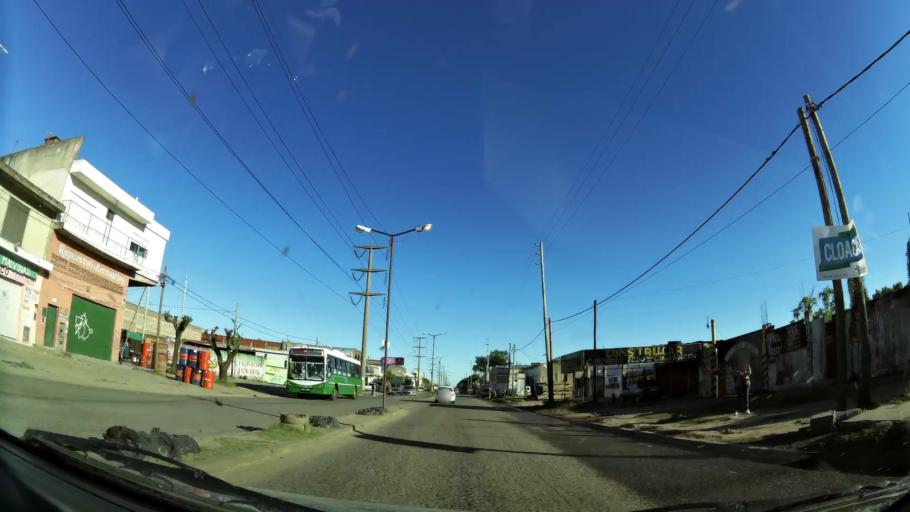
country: AR
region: Buenos Aires
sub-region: Partido de Almirante Brown
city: Adrogue
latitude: -34.7572
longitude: -58.3348
